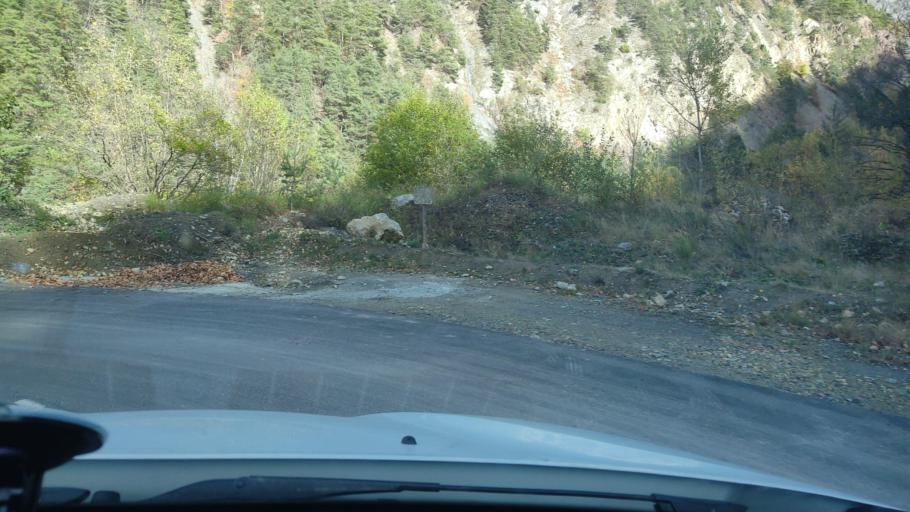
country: FR
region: Rhone-Alpes
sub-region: Departement de la Savoie
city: Saint-Jean-de-Maurienne
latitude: 45.2289
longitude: 6.3214
